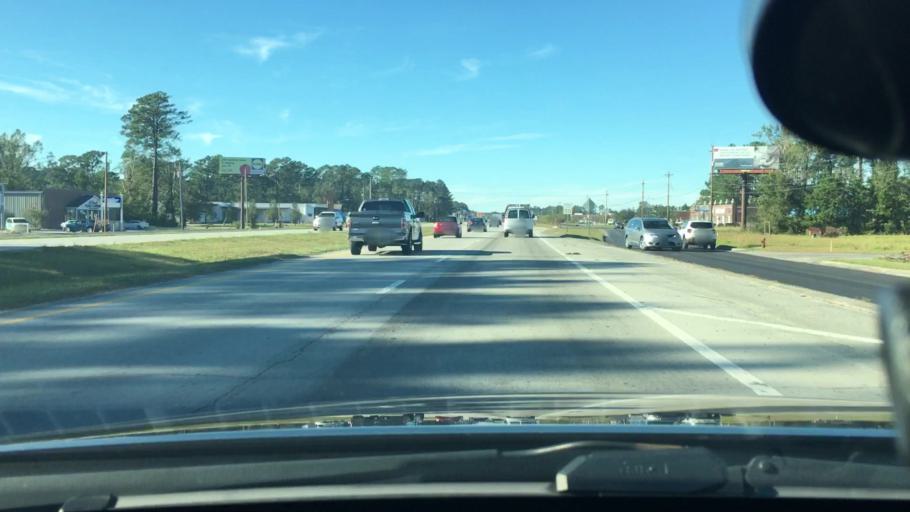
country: US
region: North Carolina
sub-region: Craven County
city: Havelock
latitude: 34.9010
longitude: -76.9305
